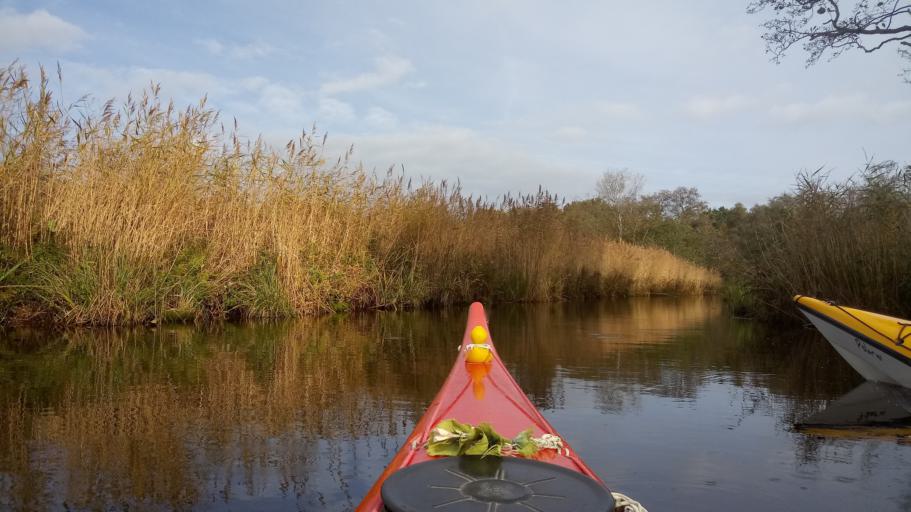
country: NL
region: Overijssel
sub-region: Gemeente Steenwijkerland
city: Sint Jansklooster
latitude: 52.6704
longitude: 6.0295
